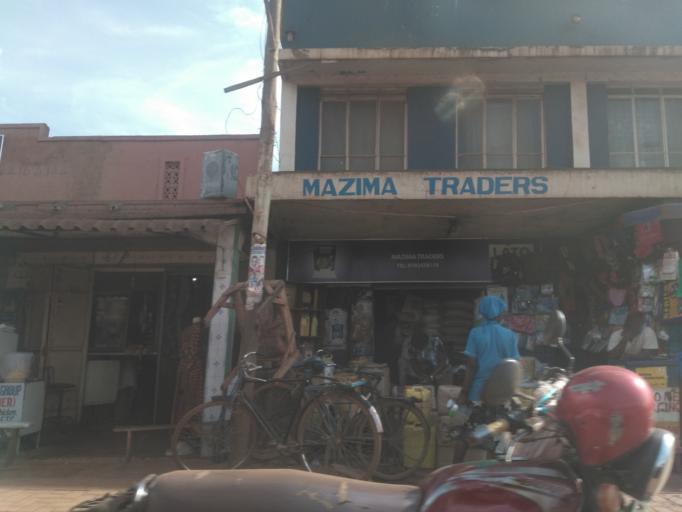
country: UG
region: Central Region
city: Kampala Central Division
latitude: 0.3528
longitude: 32.5622
